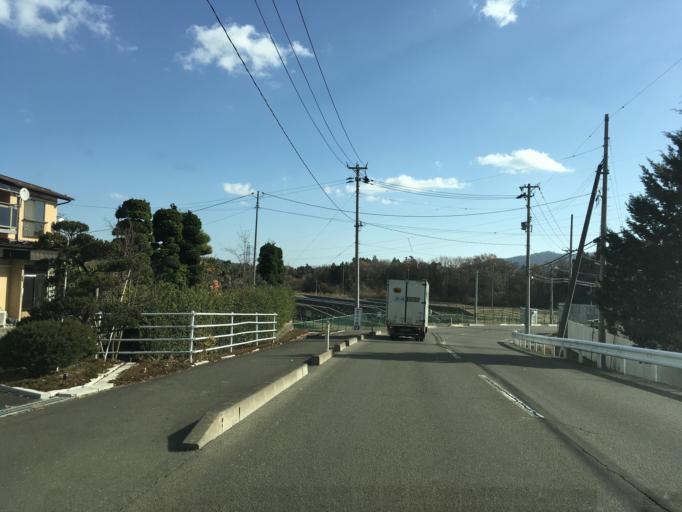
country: JP
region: Miyagi
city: Sendai
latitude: 38.2847
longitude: 140.7563
